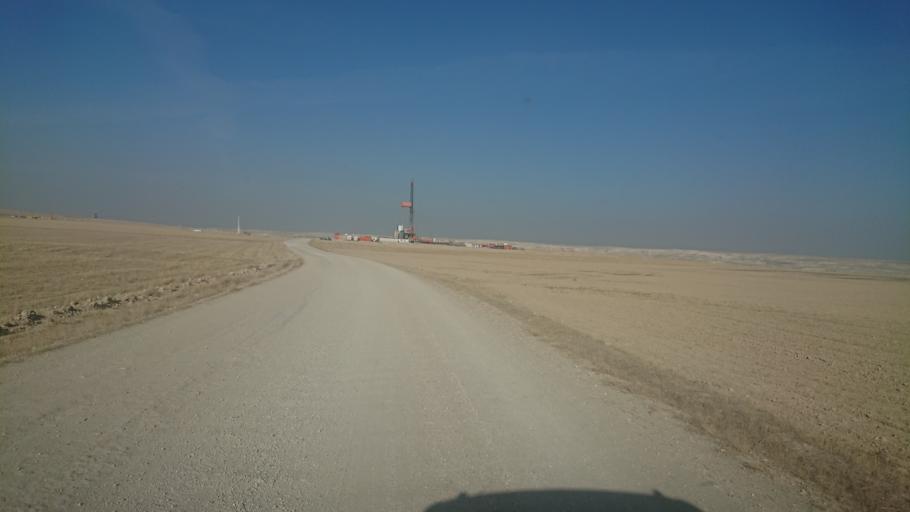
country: TR
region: Aksaray
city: Sultanhani
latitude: 38.0549
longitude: 33.6134
